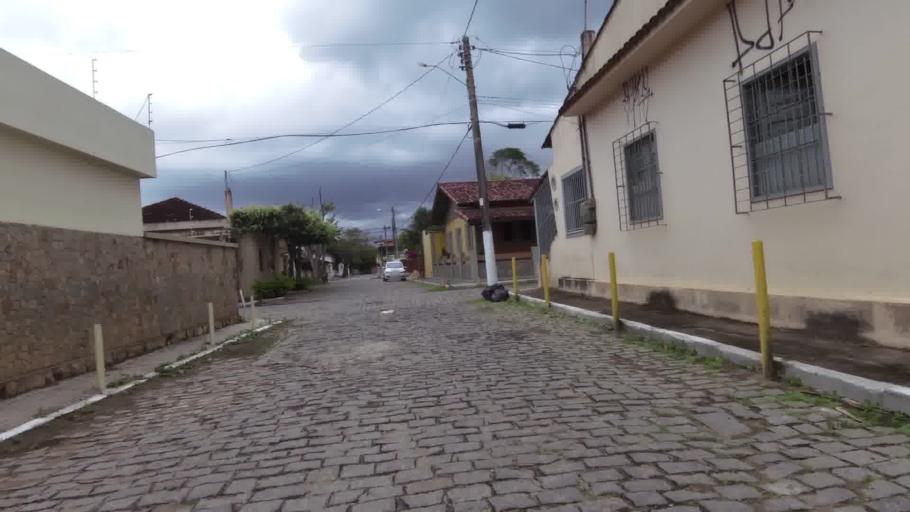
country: BR
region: Espirito Santo
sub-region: Marataizes
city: Marataizes
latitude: -21.0421
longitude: -40.8269
